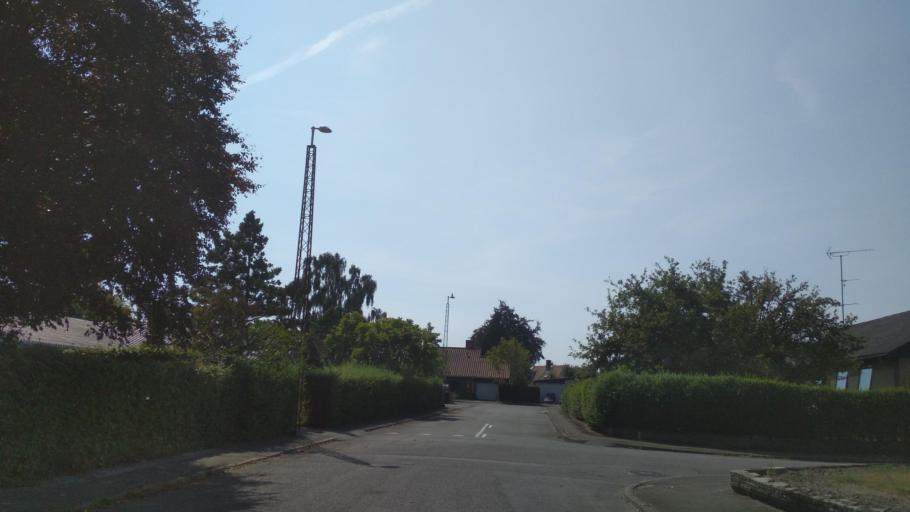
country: DK
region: Capital Region
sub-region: Bornholm Kommune
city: Akirkeby
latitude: 55.0672
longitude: 14.9276
